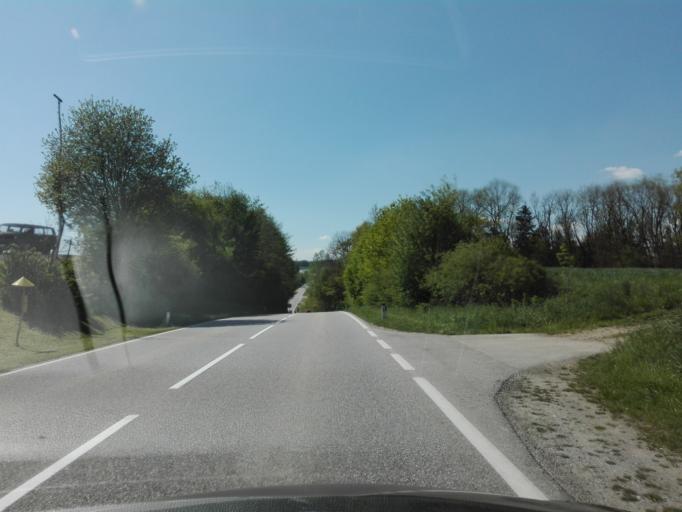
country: AT
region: Upper Austria
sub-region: Politischer Bezirk Grieskirchen
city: Bad Schallerbach
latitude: 48.3209
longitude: 13.8896
